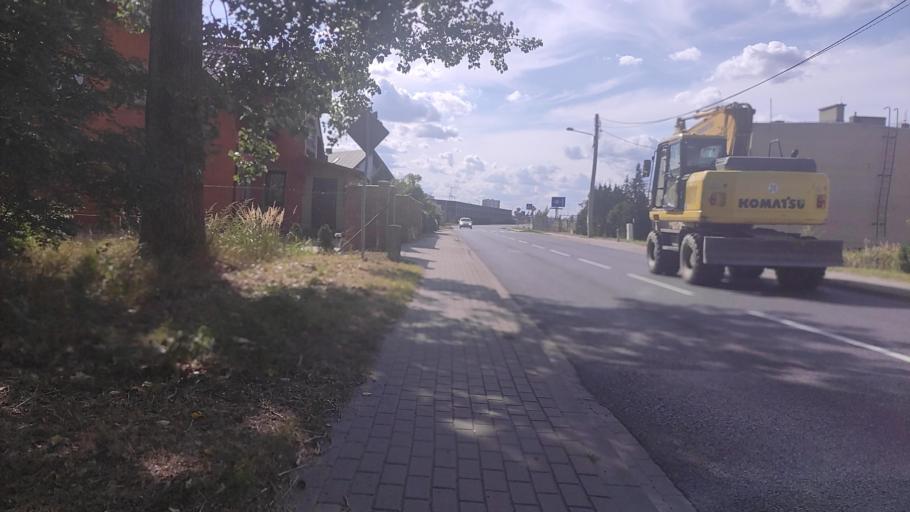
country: PL
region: Greater Poland Voivodeship
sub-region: Powiat poznanski
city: Swarzedz
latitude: 52.3978
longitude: 17.1120
